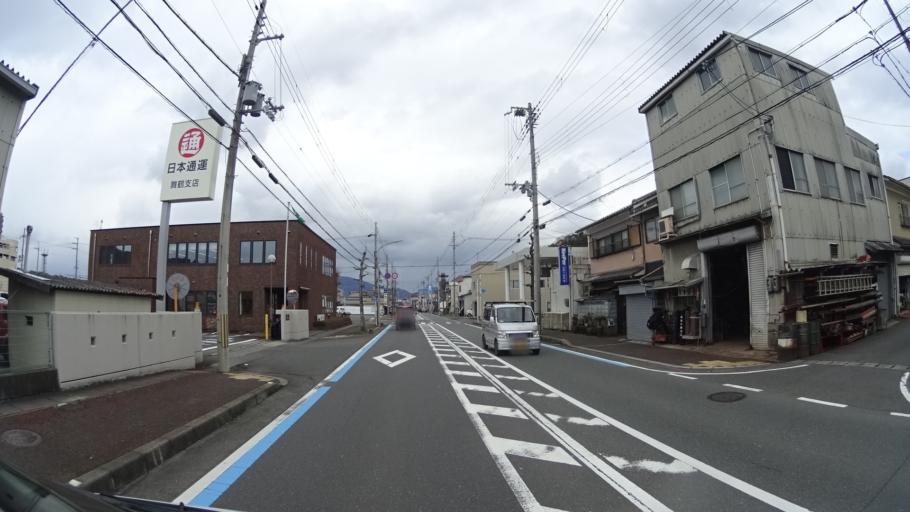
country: JP
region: Kyoto
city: Maizuru
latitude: 35.4664
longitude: 135.3974
